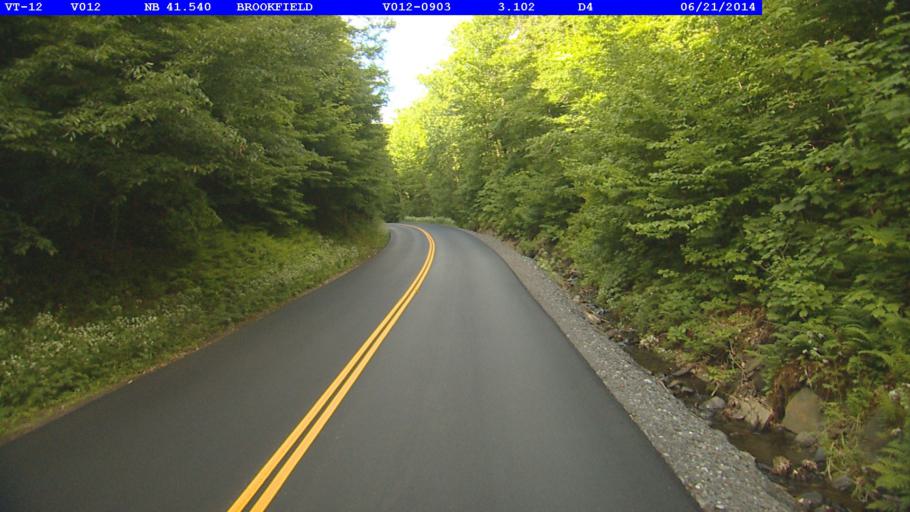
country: US
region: Vermont
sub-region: Washington County
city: Northfield
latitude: 44.0473
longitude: -72.6449
